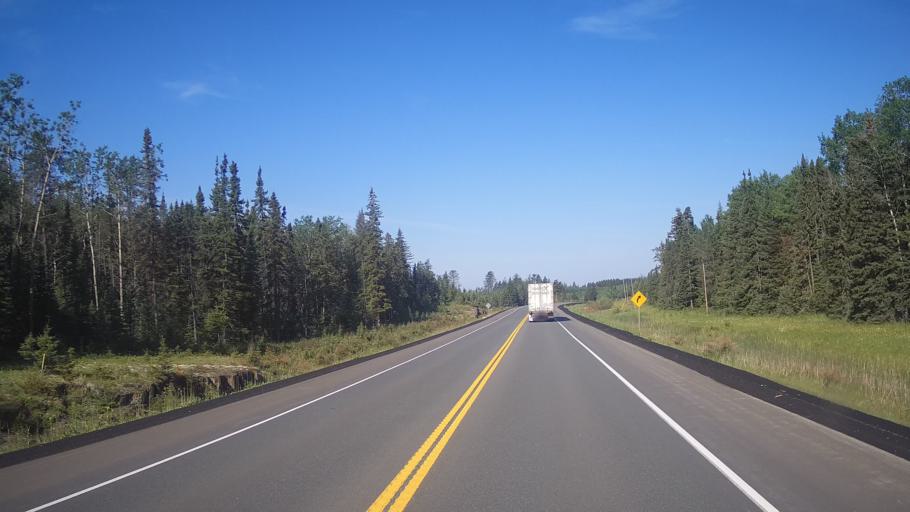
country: CA
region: Ontario
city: Dryden
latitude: 49.5837
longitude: -92.3033
